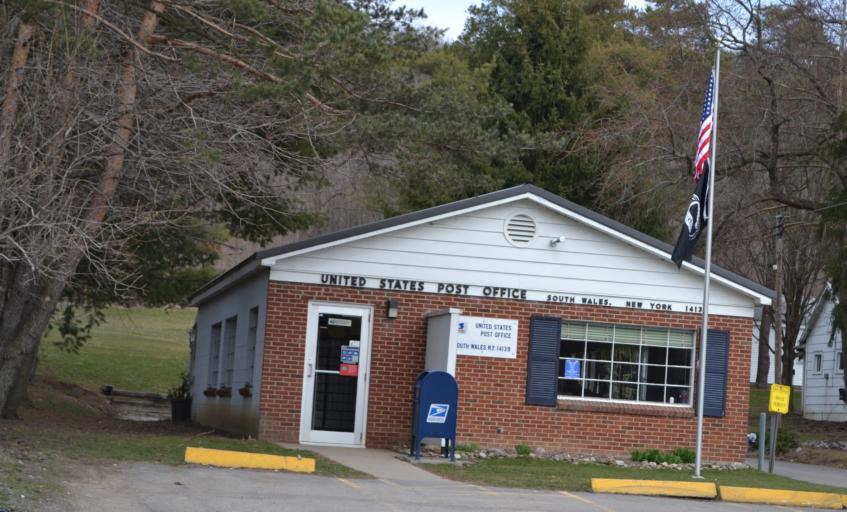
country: US
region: New York
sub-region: Erie County
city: East Aurora
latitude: 42.7073
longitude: -78.5763
